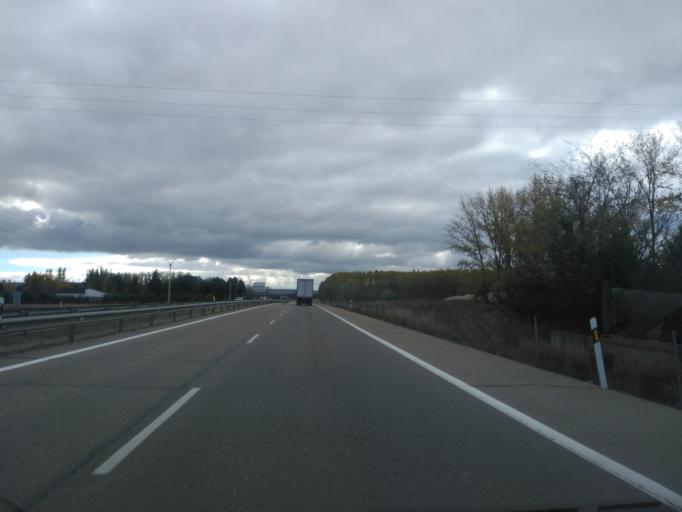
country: ES
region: Castille and Leon
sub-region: Provincia de Palencia
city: Venta de Banos
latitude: 41.9355
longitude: -4.5030
